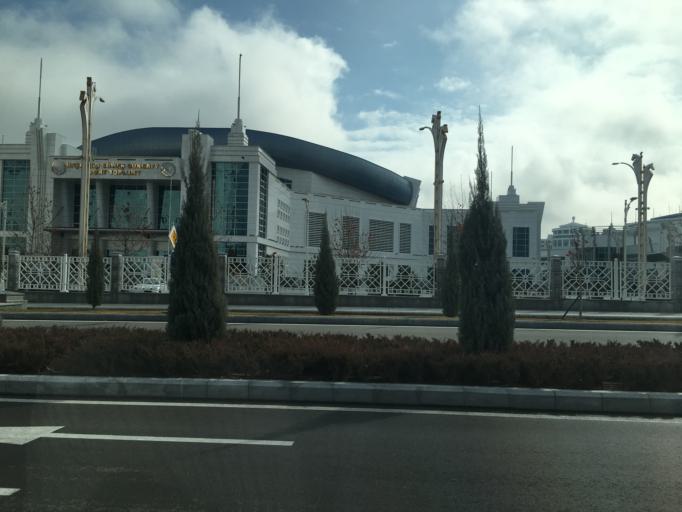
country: TM
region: Ahal
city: Ashgabat
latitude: 37.9001
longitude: 58.3717
